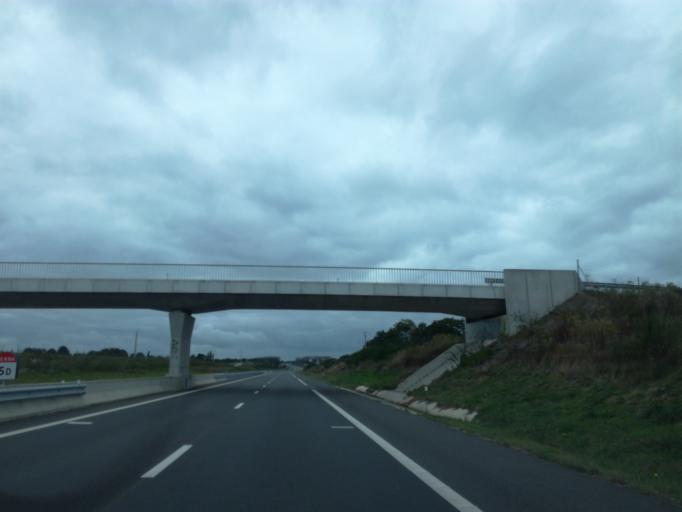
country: FR
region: Brittany
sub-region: Departement d'Ille-et-Vilaine
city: Boisgervilly
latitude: 48.1907
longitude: -2.1186
